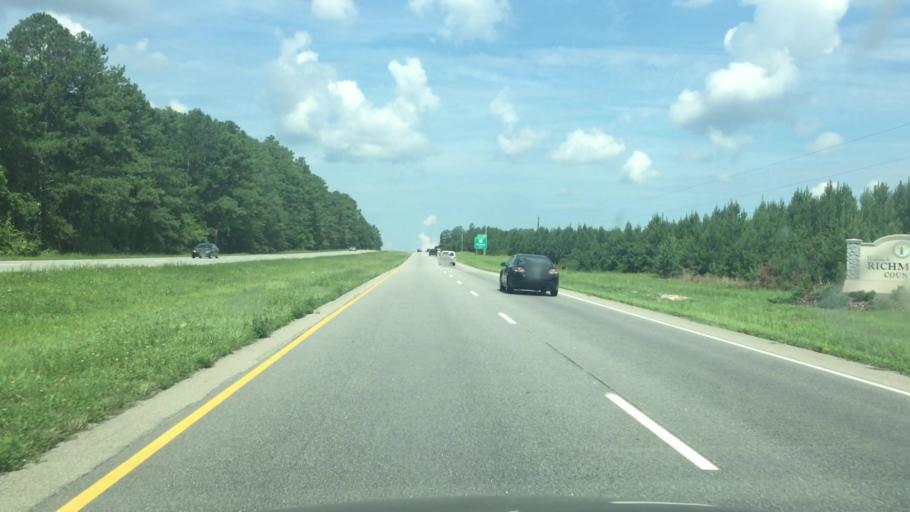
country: US
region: North Carolina
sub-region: Richmond County
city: Hamlet
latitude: 34.8586
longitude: -79.6290
